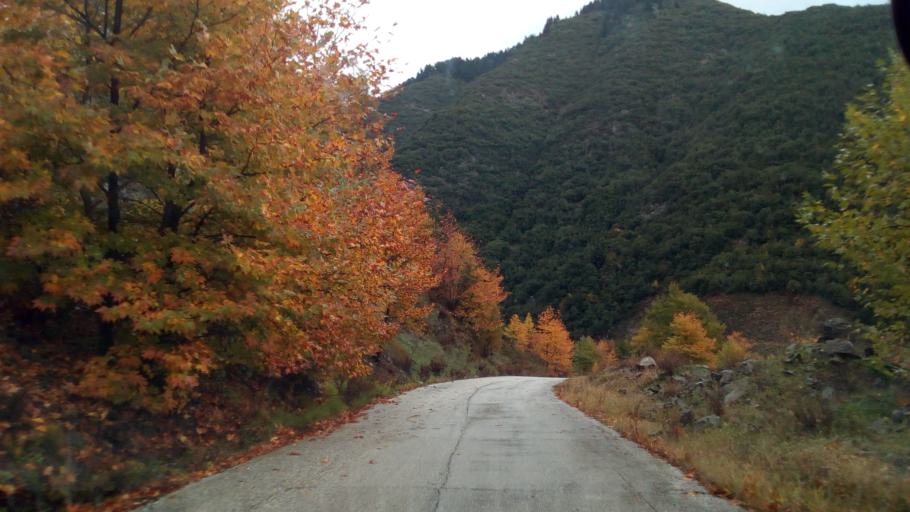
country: GR
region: West Greece
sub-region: Nomos Aitolias kai Akarnanias
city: Thermo
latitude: 38.6857
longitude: 21.8444
